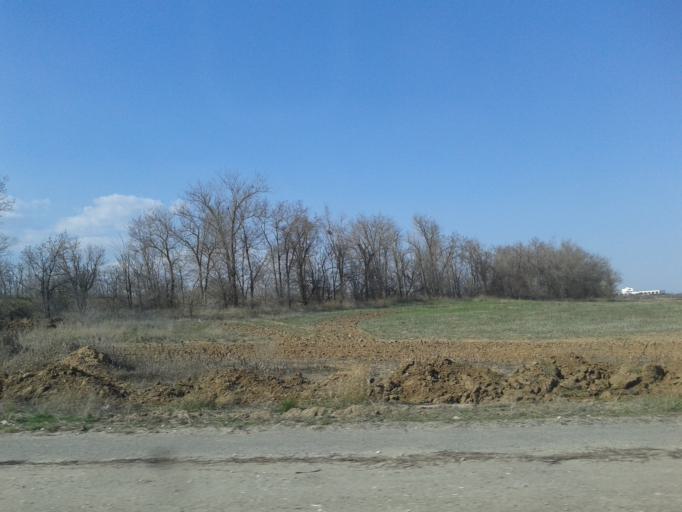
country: RU
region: Volgograd
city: Volgograd
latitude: 48.6307
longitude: 44.4116
